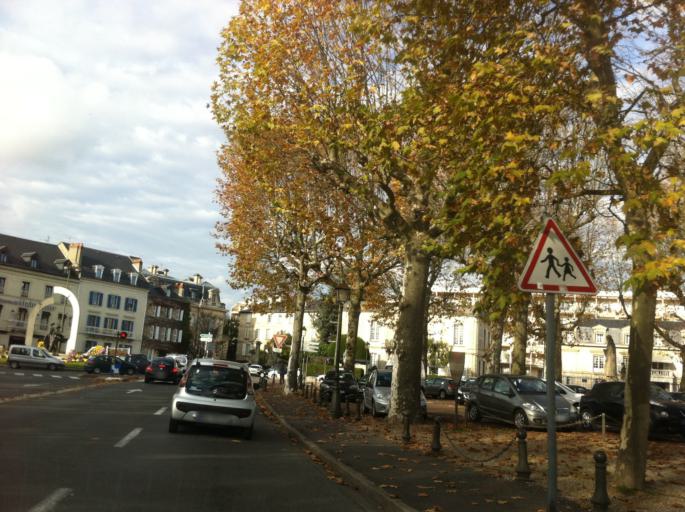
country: FR
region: Aquitaine
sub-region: Departement de la Dordogne
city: Perigueux
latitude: 45.1864
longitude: 0.7221
